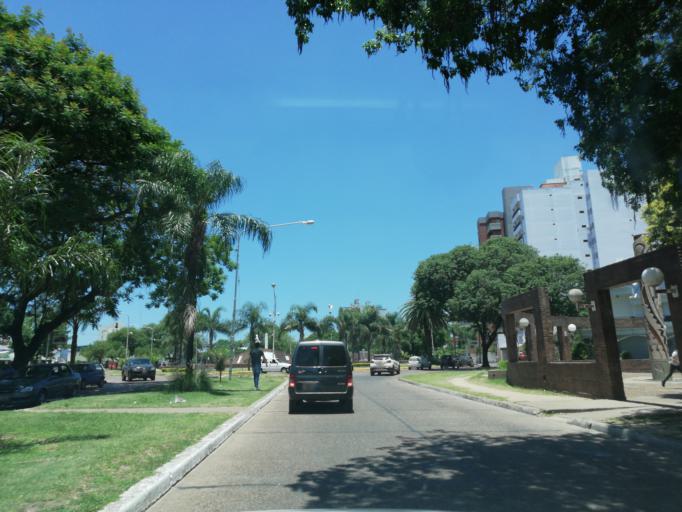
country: AR
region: Corrientes
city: Corrientes
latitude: -27.4660
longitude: -58.8230
